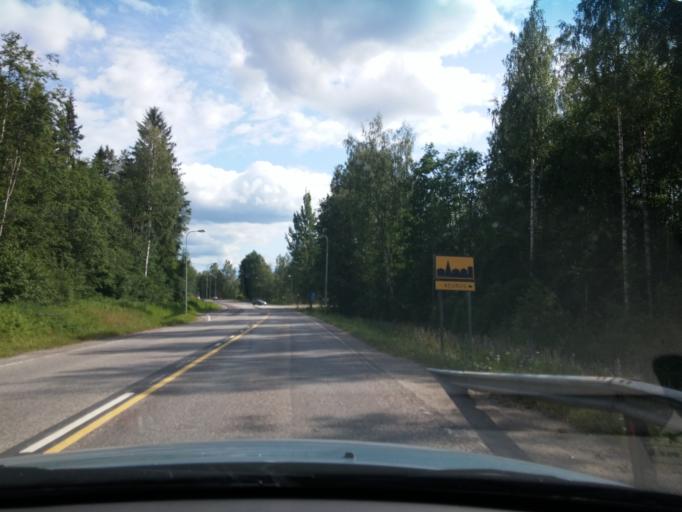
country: FI
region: Central Finland
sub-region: Keuruu
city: Keuruu
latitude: 62.2720
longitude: 24.6887
